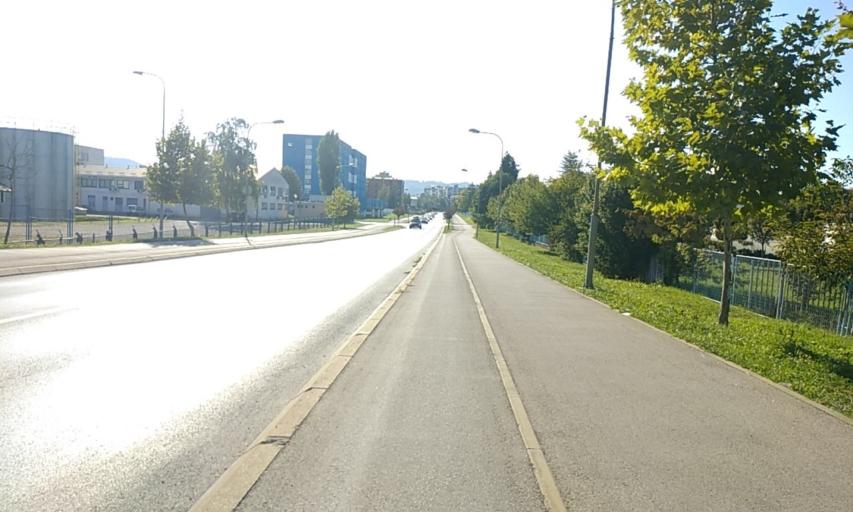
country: BA
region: Republika Srpska
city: Starcevica
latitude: 44.7730
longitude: 17.2157
